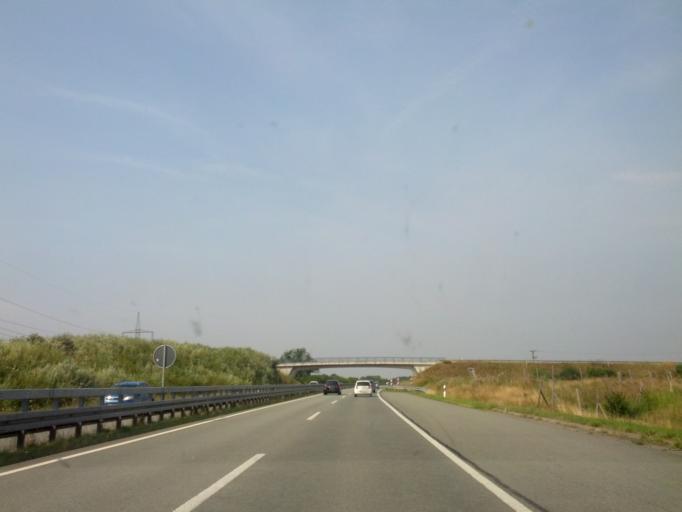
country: DE
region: Mecklenburg-Vorpommern
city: Brandshagen
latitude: 54.2044
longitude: 13.1542
